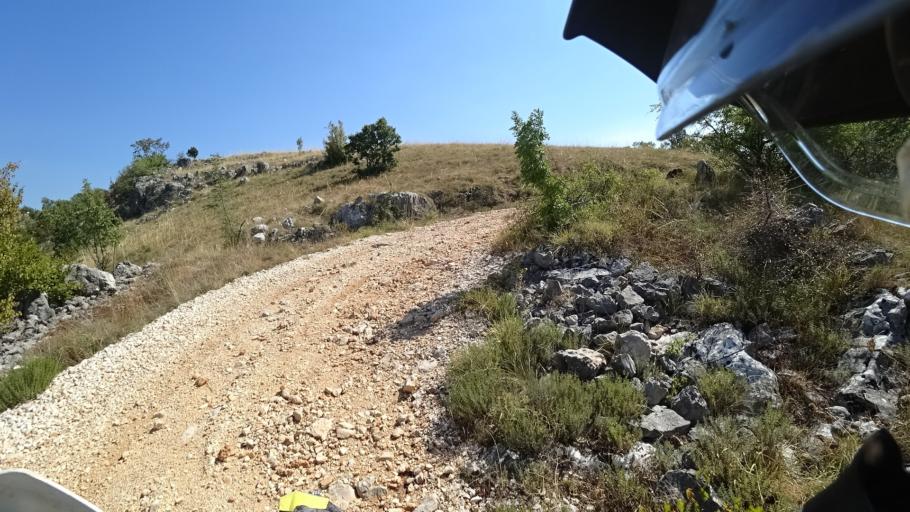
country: HR
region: Sibensko-Kniniska
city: Drnis
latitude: 43.8340
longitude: 16.2972
